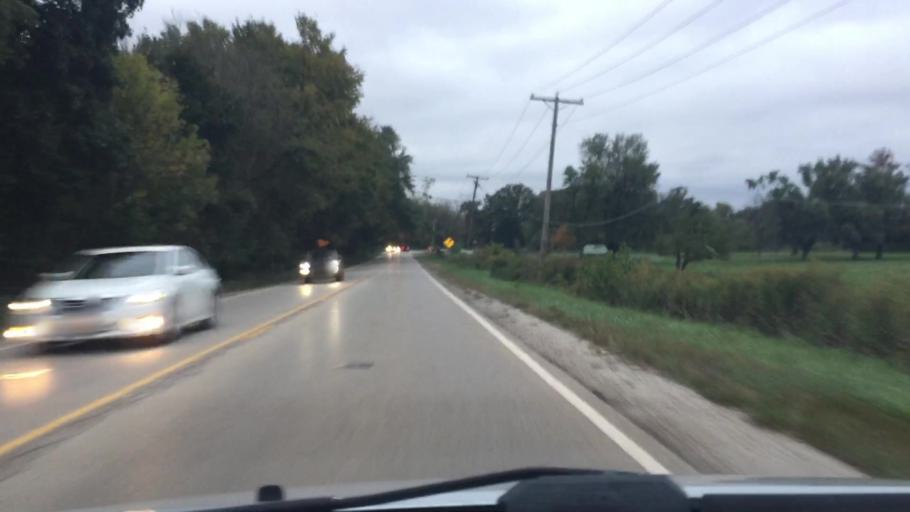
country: US
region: Illinois
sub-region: McHenry County
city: Algonquin
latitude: 42.1318
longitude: -88.3002
